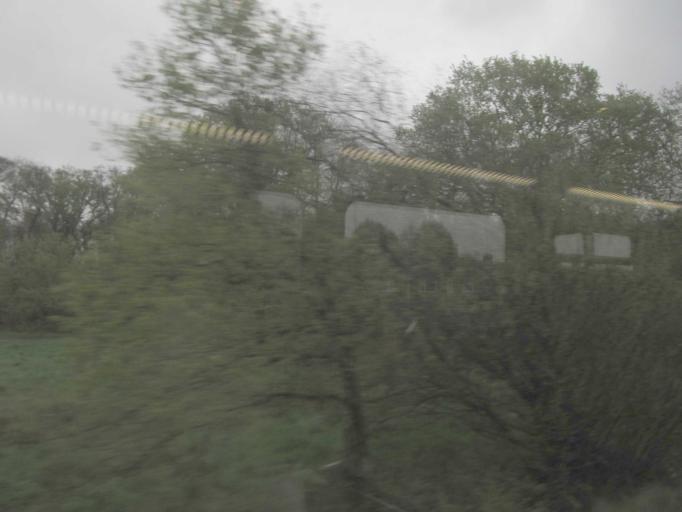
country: GB
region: England
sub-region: Bracknell Forest
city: Sandhurst
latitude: 51.3342
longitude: -0.7810
